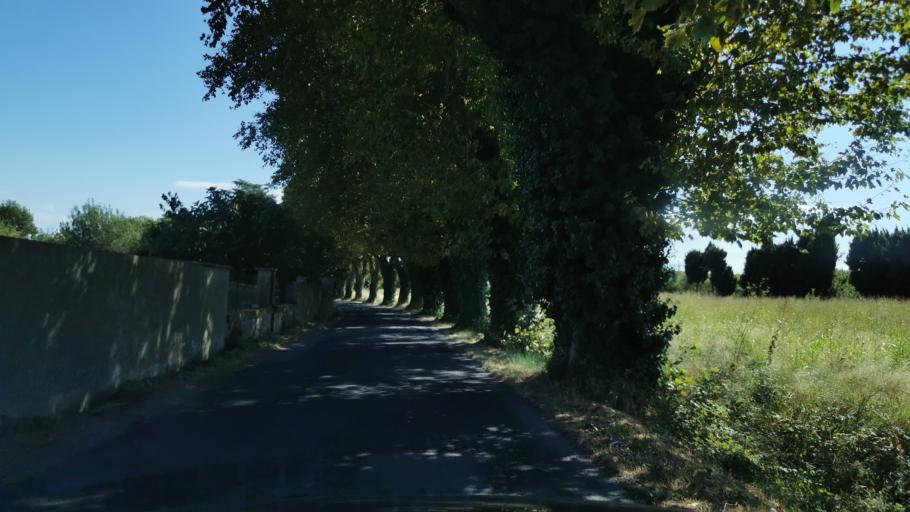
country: FR
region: Languedoc-Roussillon
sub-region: Departement de l'Aude
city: Peyriac-Minervois
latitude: 43.2952
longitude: 2.5683
